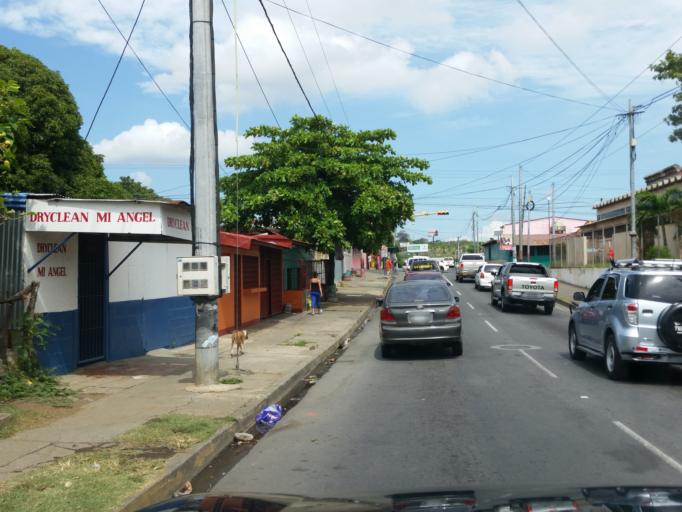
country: NI
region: Managua
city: Managua
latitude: 12.1082
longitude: -86.2969
